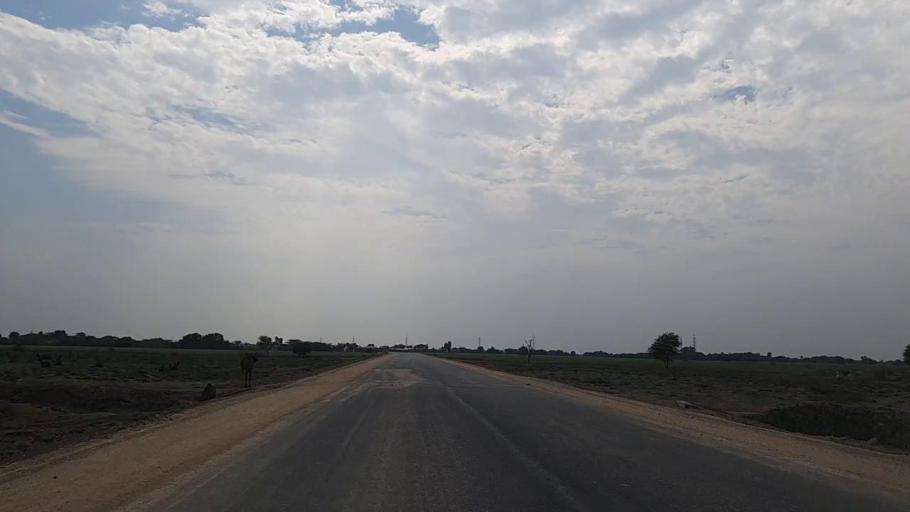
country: PK
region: Sindh
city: Naukot
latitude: 24.9724
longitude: 69.2846
